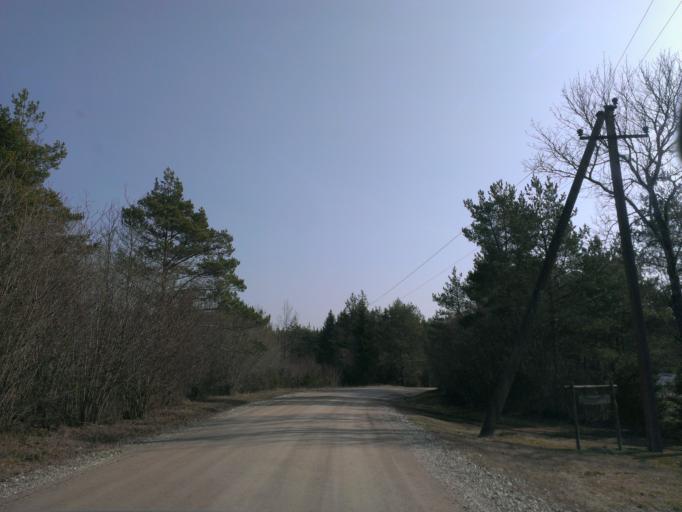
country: EE
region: Saare
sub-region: Kuressaare linn
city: Kuressaare
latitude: 58.3792
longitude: 22.7233
